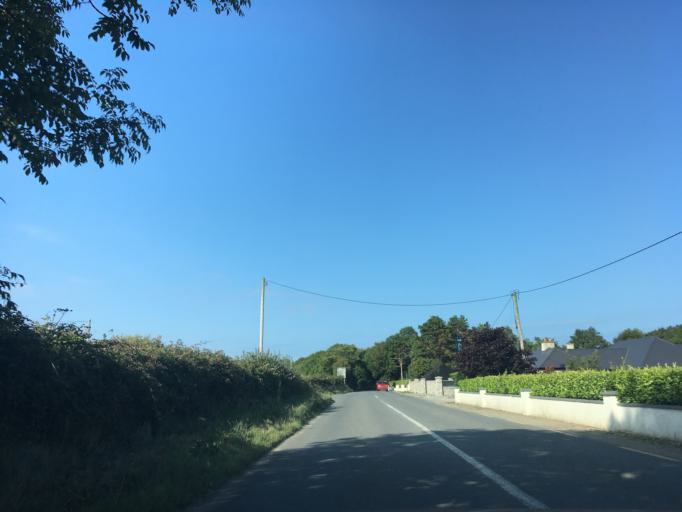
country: IE
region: Leinster
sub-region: Loch Garman
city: Loch Garman
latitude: 52.2657
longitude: -6.4796
